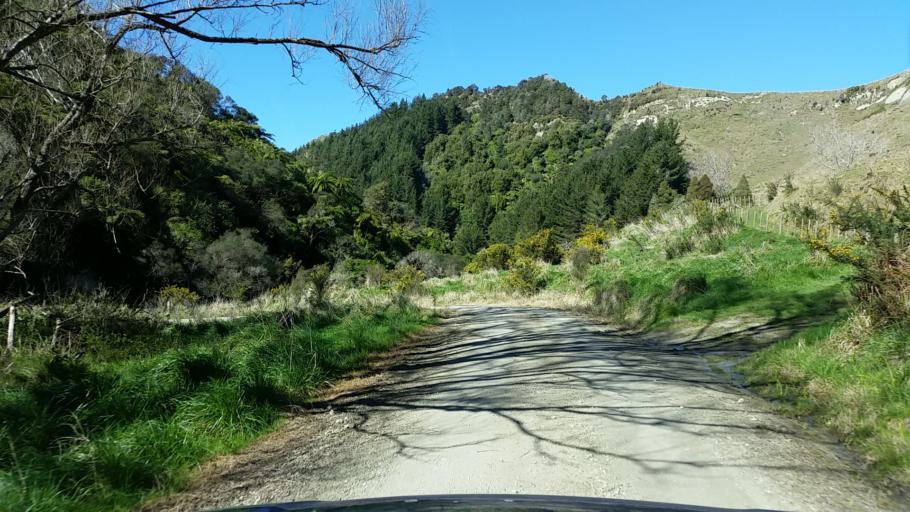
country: NZ
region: Manawatu-Wanganui
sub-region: Wanganui District
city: Wanganui
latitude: -39.6692
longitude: 174.8651
